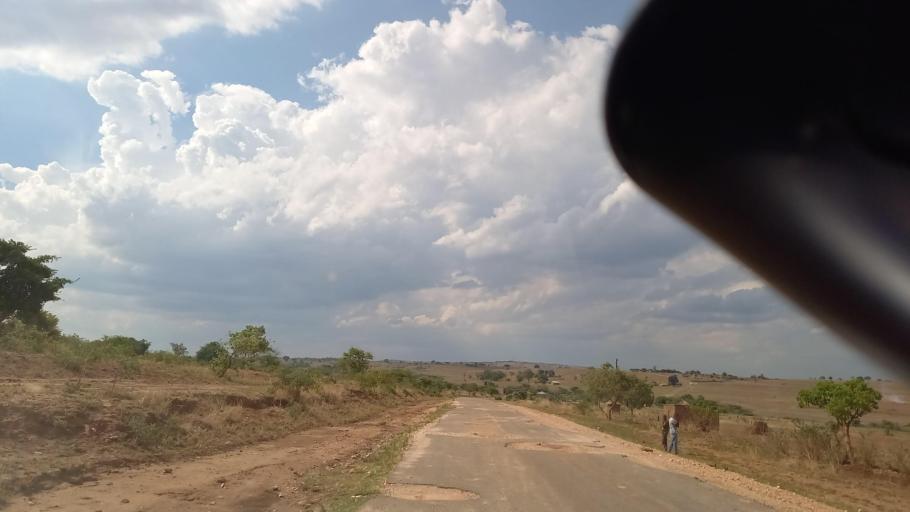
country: ZM
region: Lusaka
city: Kafue
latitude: -16.2145
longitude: 28.1132
